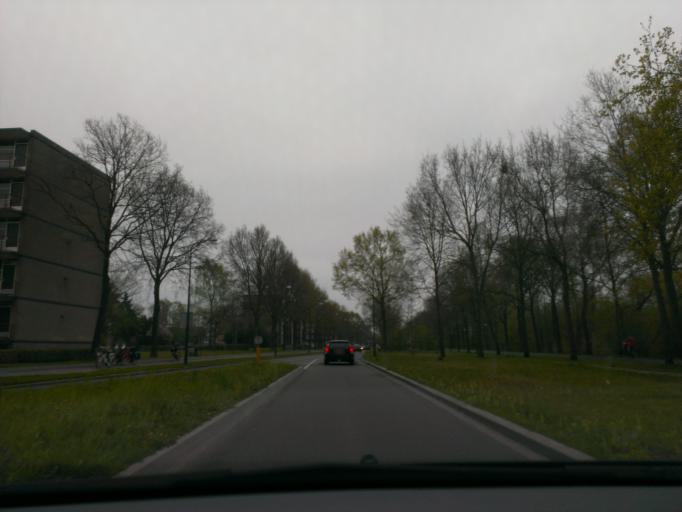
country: NL
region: Gelderland
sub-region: Gemeente Apeldoorn
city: Apeldoorn
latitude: 52.2257
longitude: 5.9897
